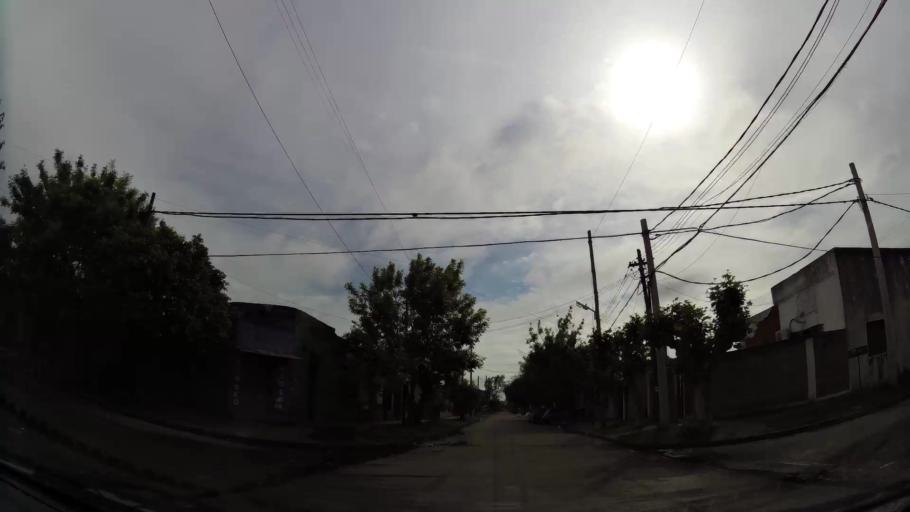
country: AR
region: Buenos Aires
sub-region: Partido de Quilmes
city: Quilmes
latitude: -34.7178
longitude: -58.2451
